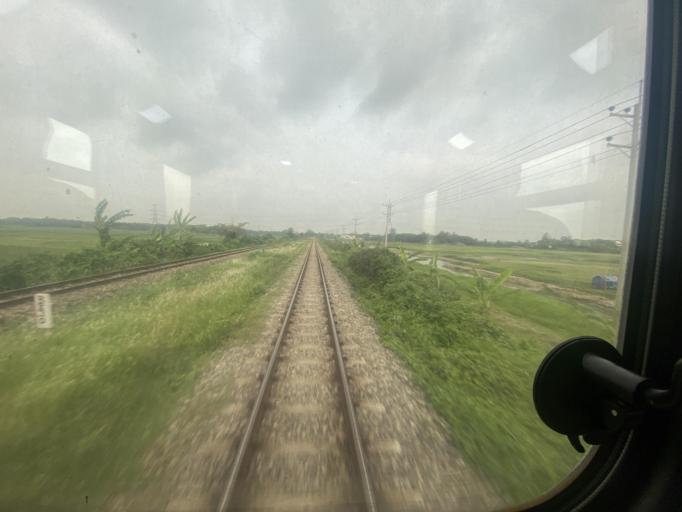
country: BD
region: Dhaka
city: Tungi
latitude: 23.9333
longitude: 90.5046
